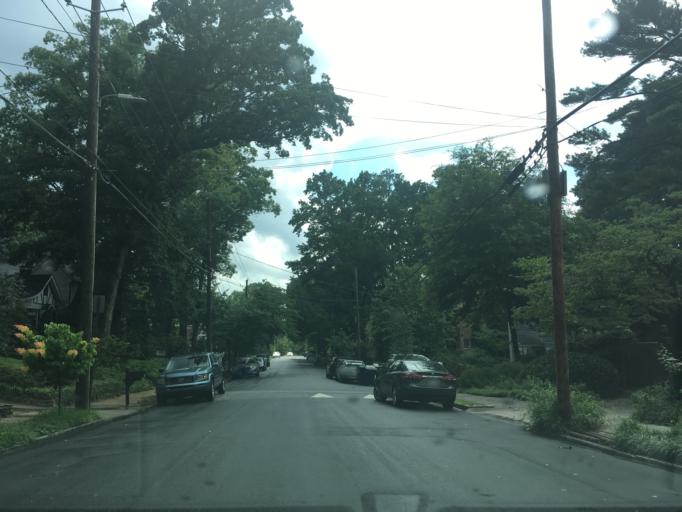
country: US
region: Georgia
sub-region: DeKalb County
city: Druid Hills
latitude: 33.7876
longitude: -84.3579
